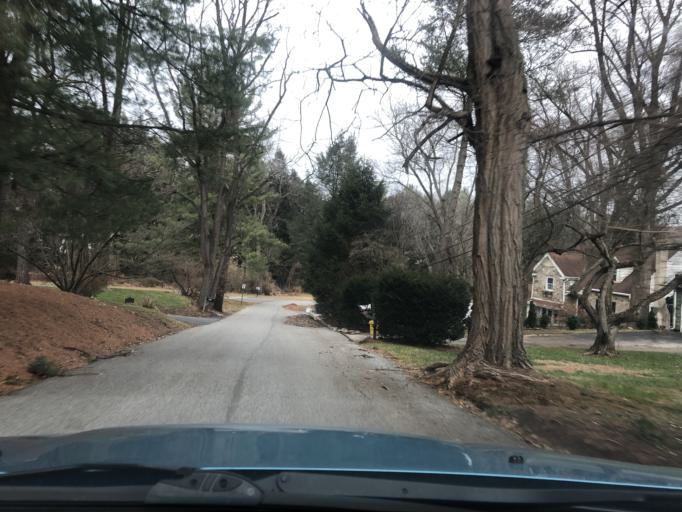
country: US
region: Pennsylvania
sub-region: Delaware County
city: Radnor
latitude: 40.0265
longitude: -75.3675
